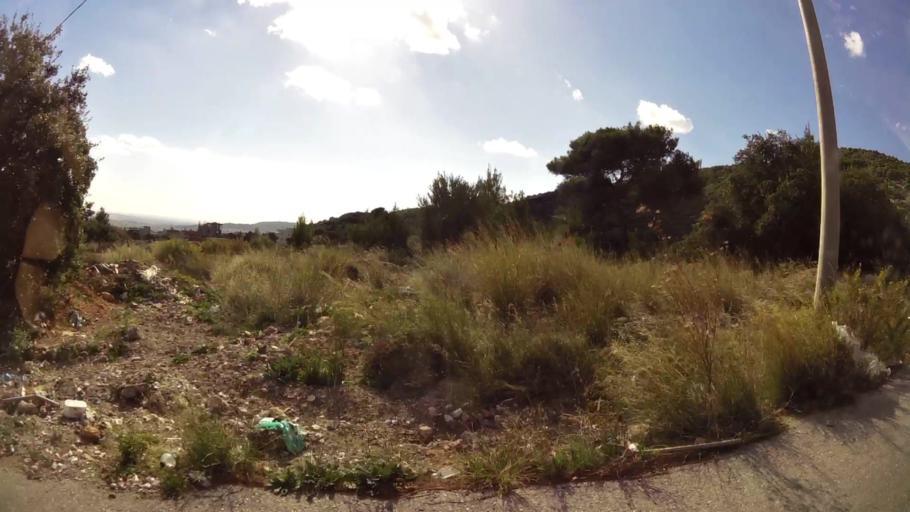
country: GR
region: Attica
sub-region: Nomarchia Anatolikis Attikis
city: Acharnes
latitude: 38.1167
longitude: 23.7235
